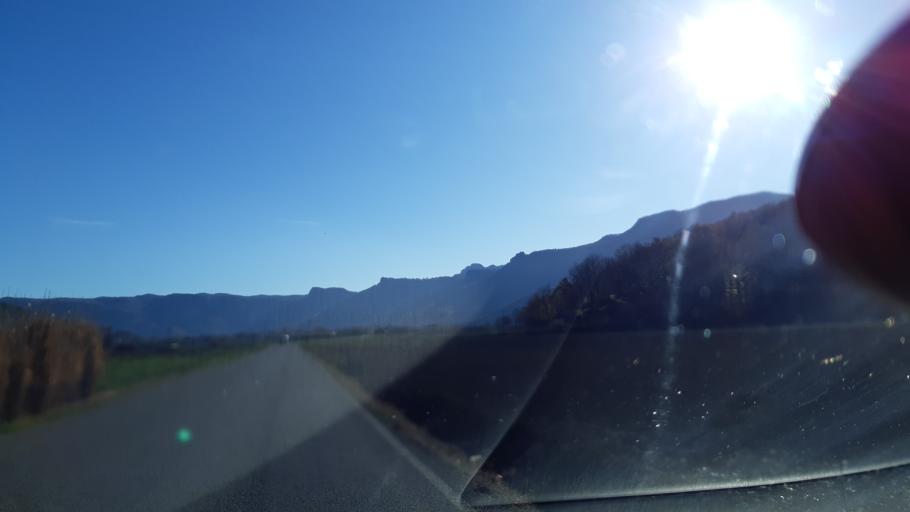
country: ES
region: Catalonia
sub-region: Provincia de Girona
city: Bas
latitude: 42.1406
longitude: 2.4409
